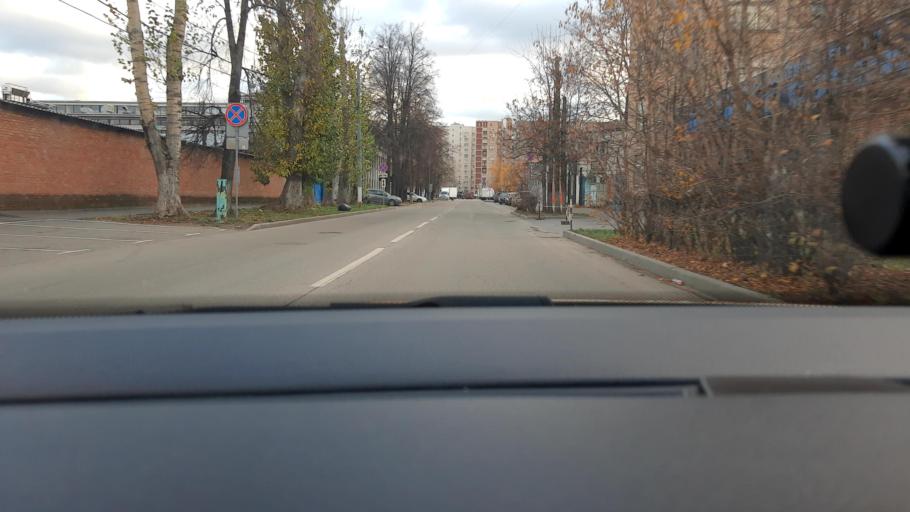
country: RU
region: Moscow
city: Ryazanskiy
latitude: 55.7514
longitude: 37.7694
